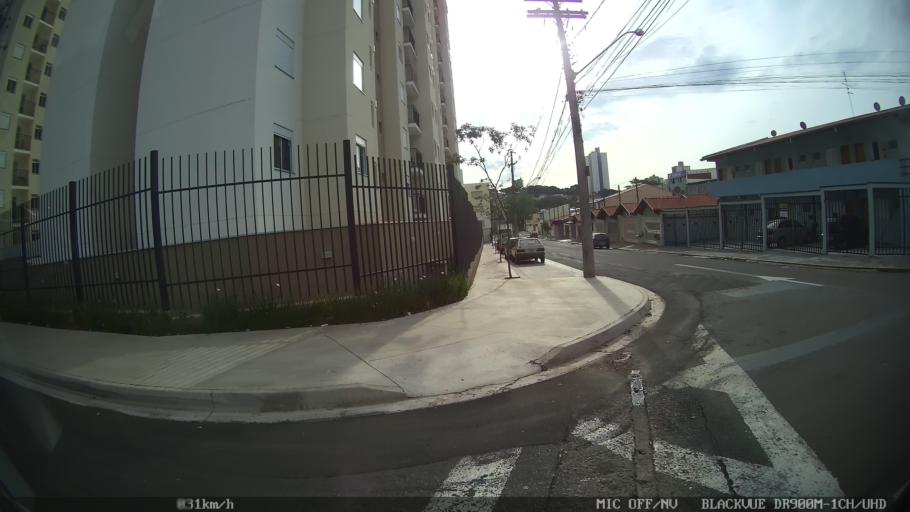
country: BR
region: Sao Paulo
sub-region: Piracicaba
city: Piracicaba
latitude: -22.7351
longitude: -47.6269
